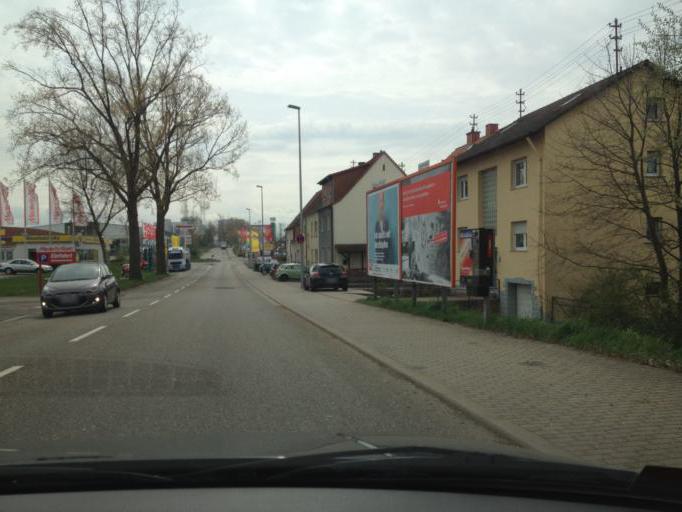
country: DE
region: Rheinland-Pfalz
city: Petersberg
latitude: 49.2271
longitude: 7.5893
